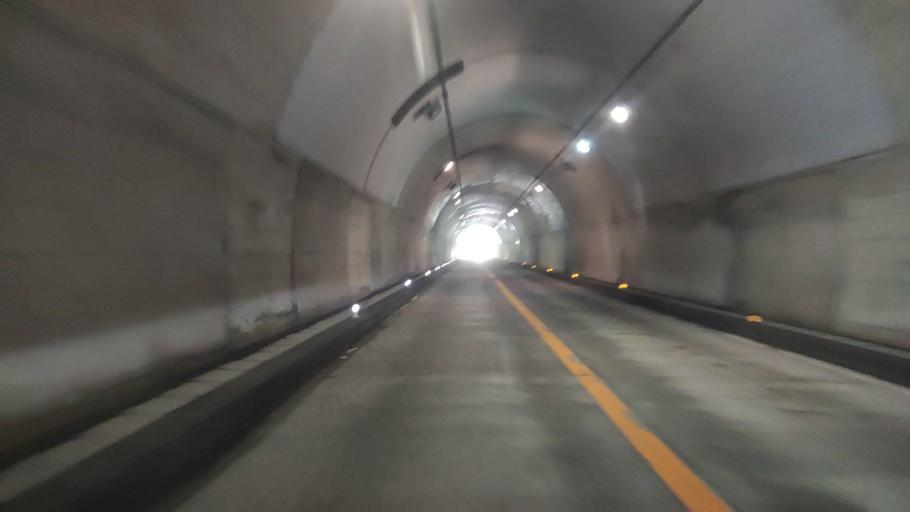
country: JP
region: Wakayama
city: Shingu
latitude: 33.8164
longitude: 135.8564
